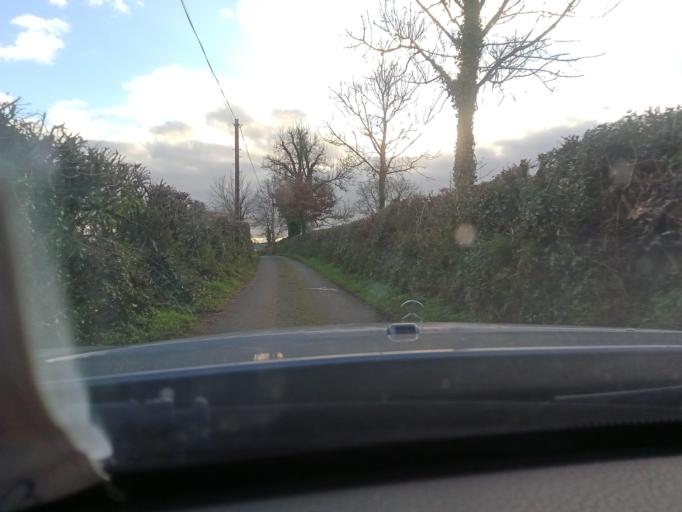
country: IE
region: Leinster
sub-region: Kilkenny
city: Graiguenamanagh
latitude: 52.5089
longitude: -6.9413
